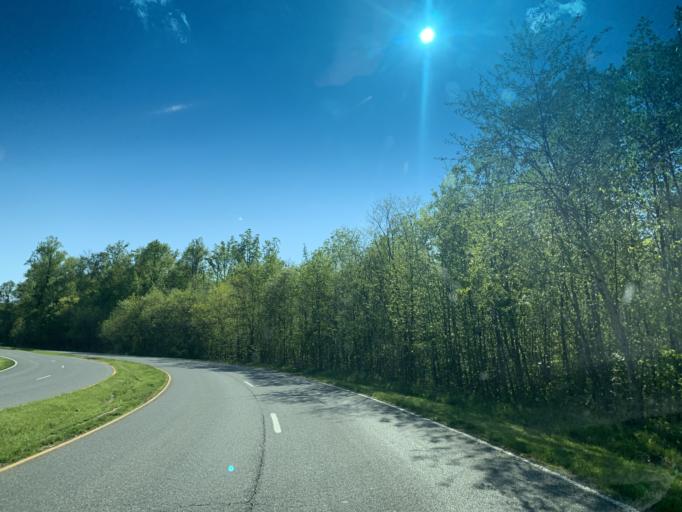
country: US
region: Maryland
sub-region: Harford County
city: Aberdeen
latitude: 39.5336
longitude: -76.1936
